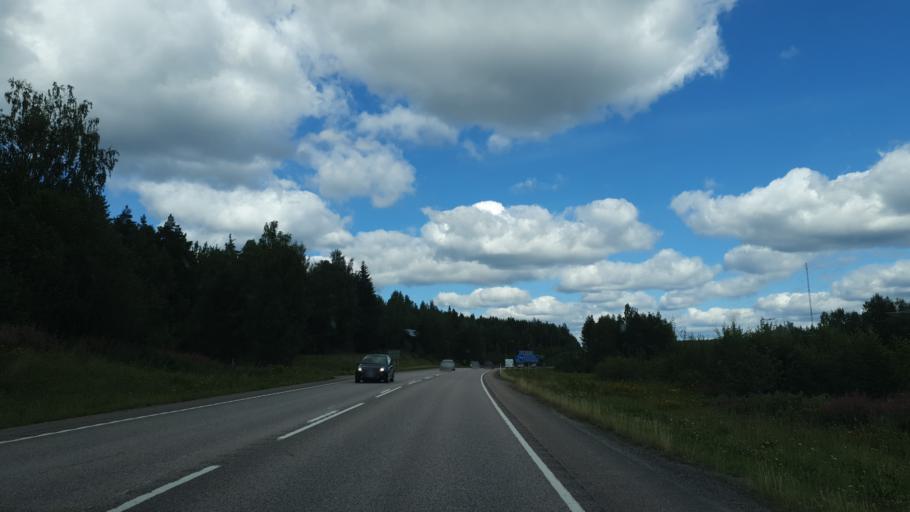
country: FI
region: Pirkanmaa
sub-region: Tampere
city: Kuhmalahti
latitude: 61.7215
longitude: 24.6513
